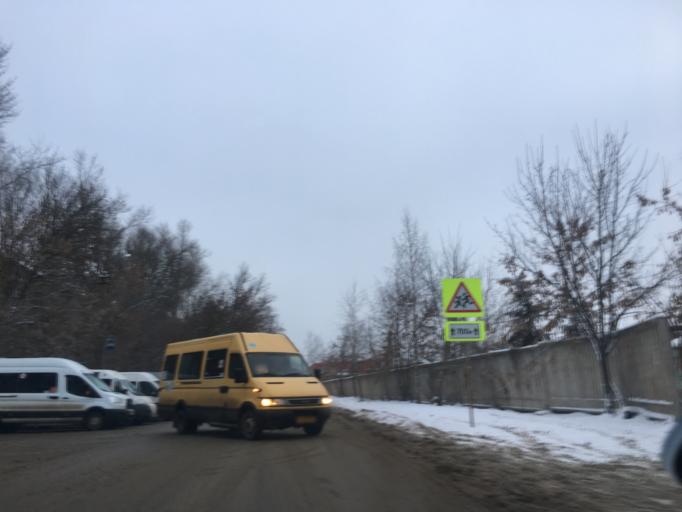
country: RU
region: Tula
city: Mendeleyevskiy
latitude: 54.1754
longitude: 37.5658
